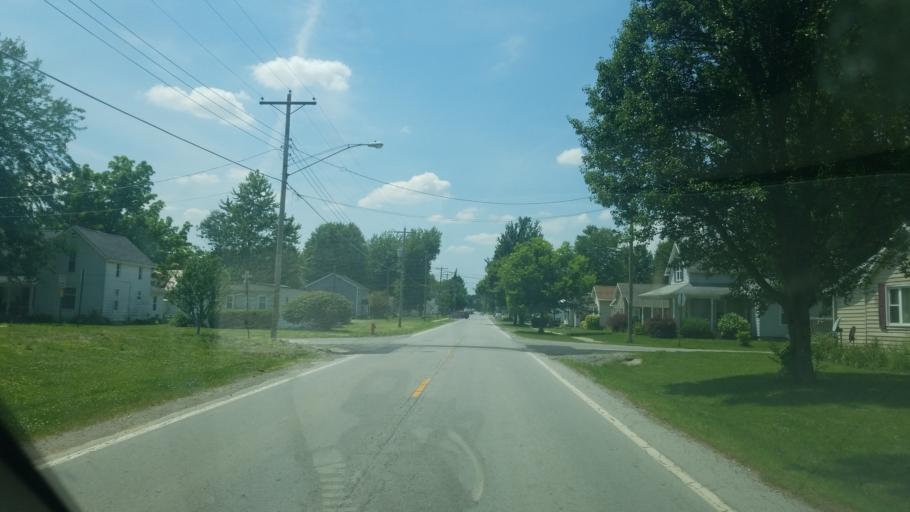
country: US
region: Ohio
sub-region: Hardin County
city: Ada
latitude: 40.7767
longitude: -83.8197
